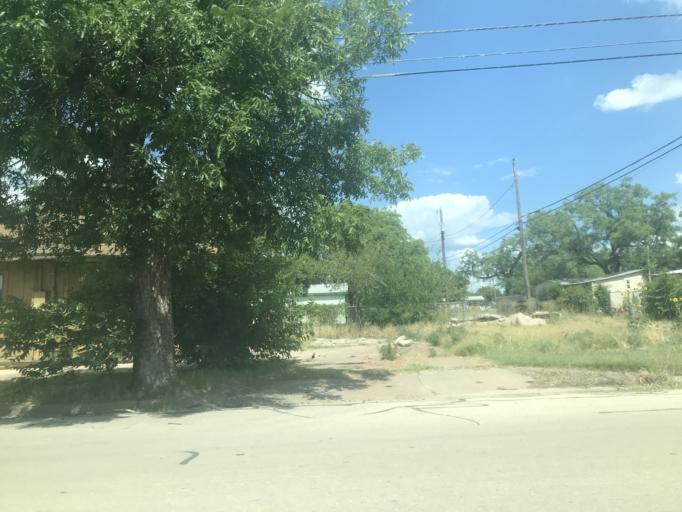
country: US
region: Texas
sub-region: Taylor County
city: Abilene
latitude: 32.4282
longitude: -99.7525
